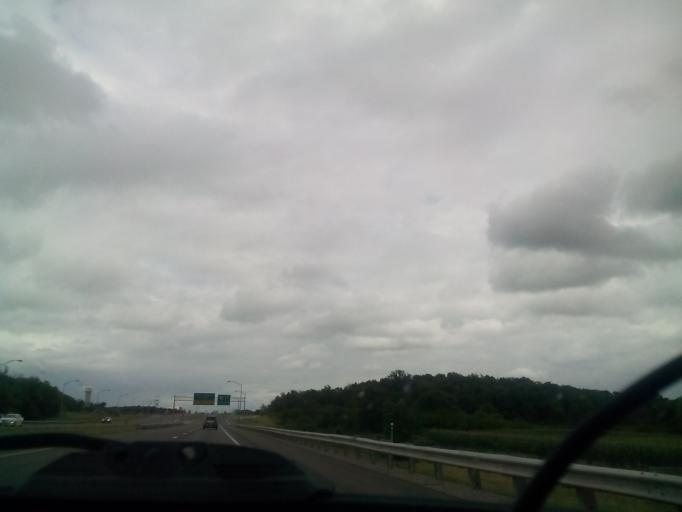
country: US
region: Indiana
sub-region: Steuben County
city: Hamilton
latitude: 41.6301
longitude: -84.7756
